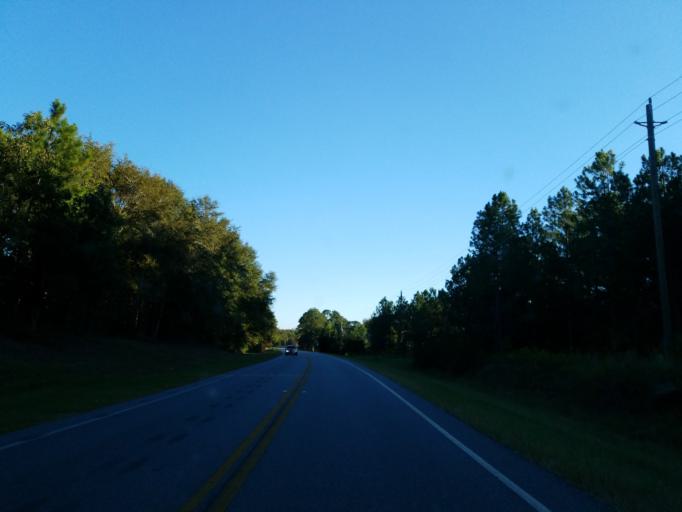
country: US
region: Georgia
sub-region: Worth County
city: Sylvester
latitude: 31.5746
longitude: -83.8548
